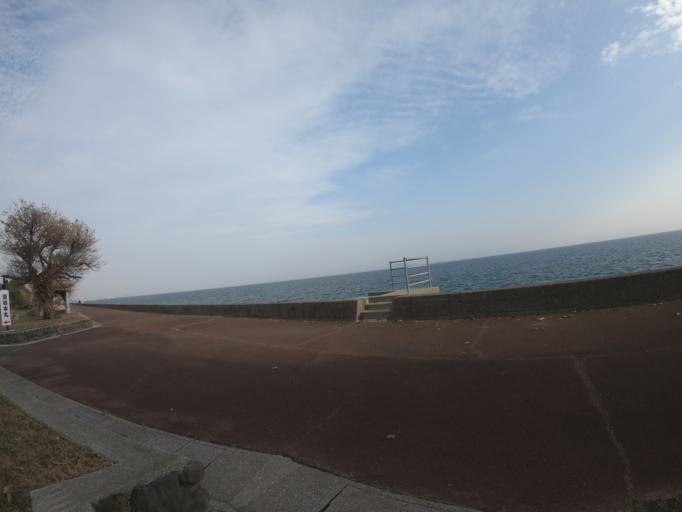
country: JP
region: Nagasaki
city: Shimabara
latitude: 32.6316
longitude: 130.2572
